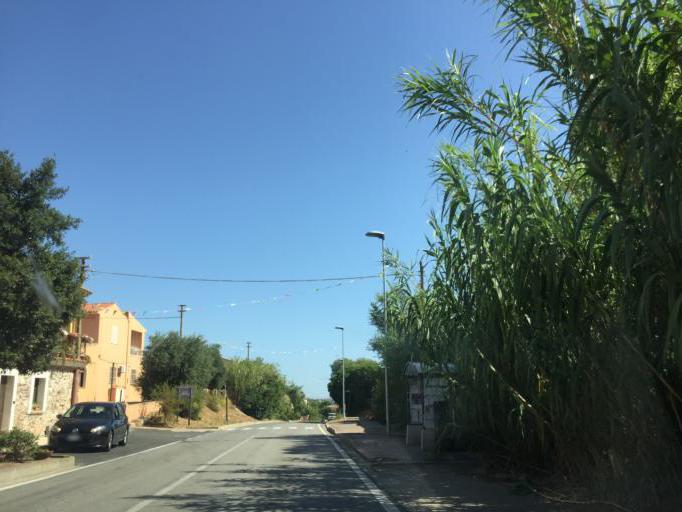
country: IT
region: Sardinia
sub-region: Provincia di Olbia-Tempio
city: San Teodoro
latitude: 40.7437
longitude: 9.6466
